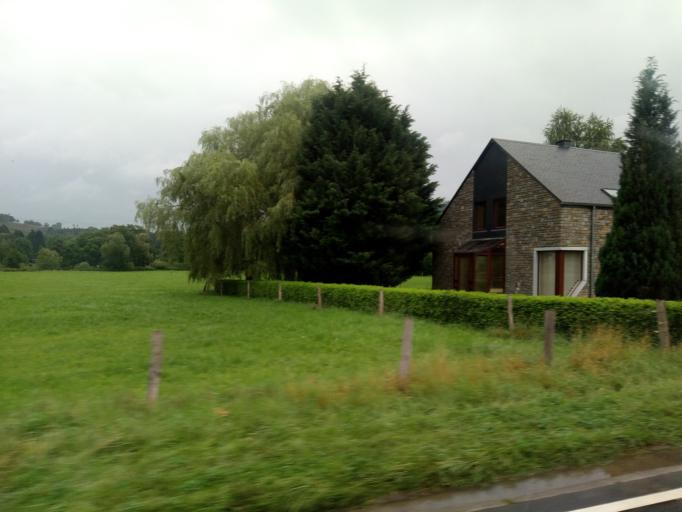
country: BE
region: Wallonia
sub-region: Province du Luxembourg
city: Hotton
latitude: 50.2554
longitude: 5.4772
